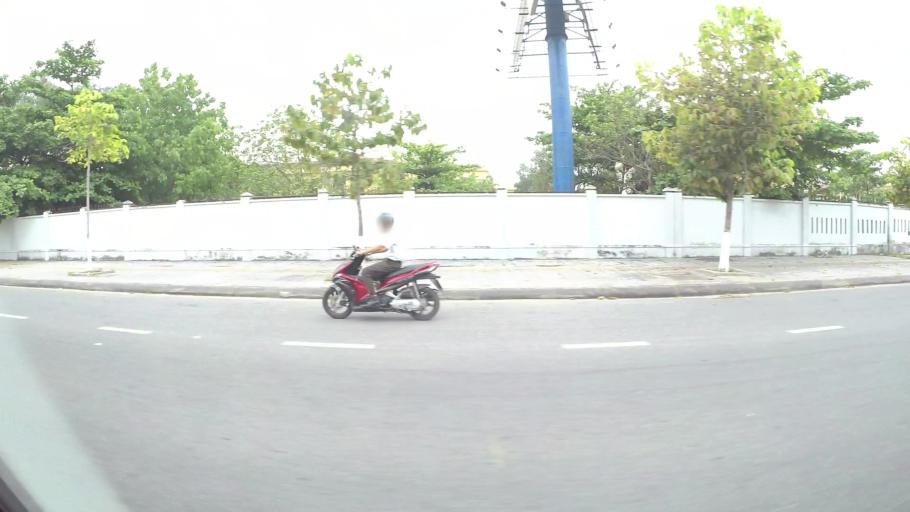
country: VN
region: Da Nang
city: Da Nang
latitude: 16.0504
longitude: 108.2059
